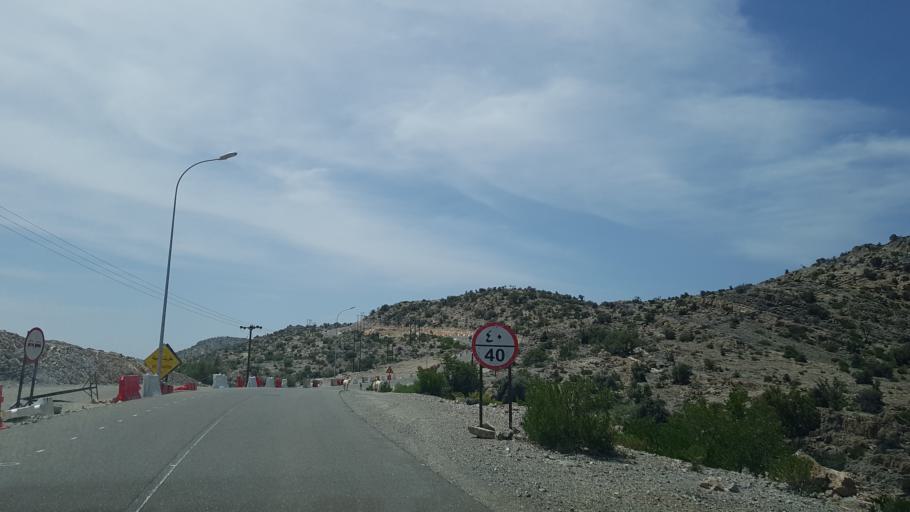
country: OM
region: Muhafazat ad Dakhiliyah
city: Nizwa
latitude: 23.1154
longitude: 57.6444
